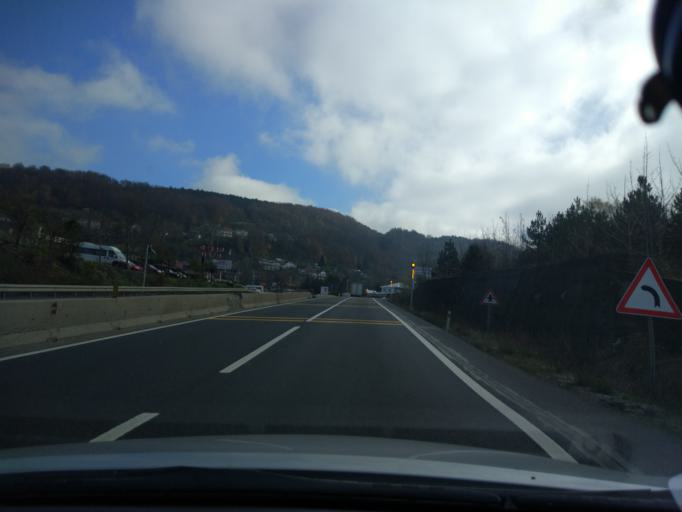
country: TR
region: Duzce
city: Kaynasli
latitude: 40.7476
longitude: 31.3786
